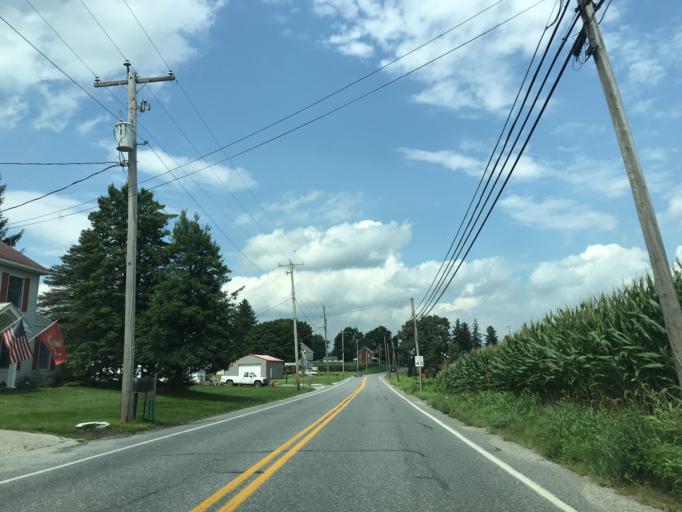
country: US
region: Pennsylvania
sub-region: York County
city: Red Lion
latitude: 39.8444
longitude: -76.6208
